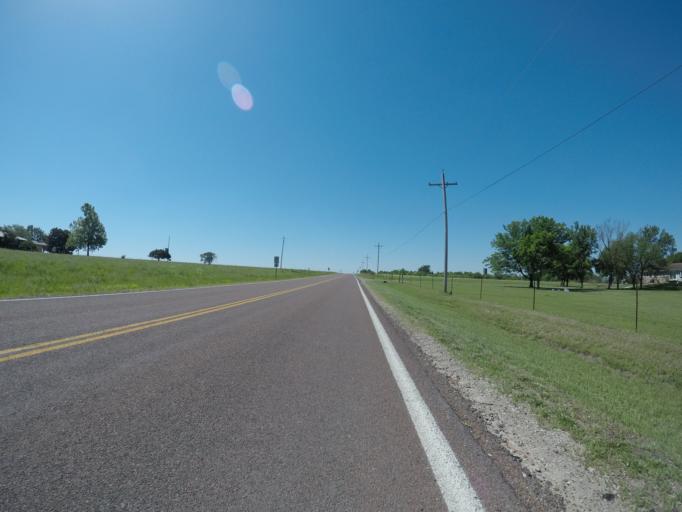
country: US
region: Kansas
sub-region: Morris County
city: Council Grove
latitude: 38.8394
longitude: -96.5941
